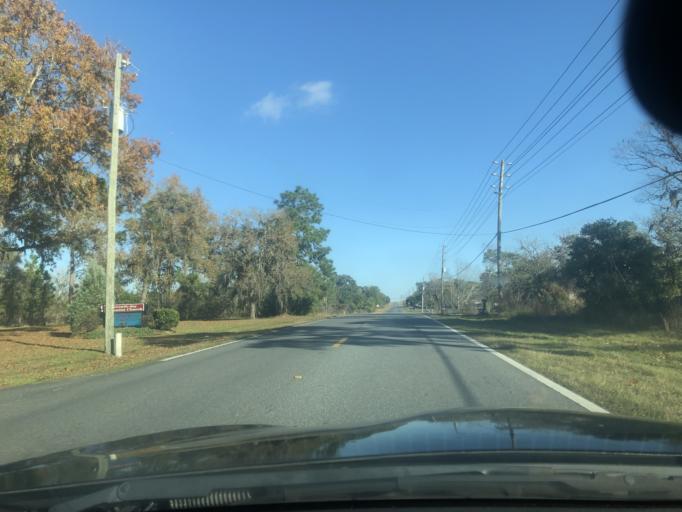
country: US
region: Florida
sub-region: Citrus County
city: Sugarmill Woods
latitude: 28.7640
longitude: -82.5313
